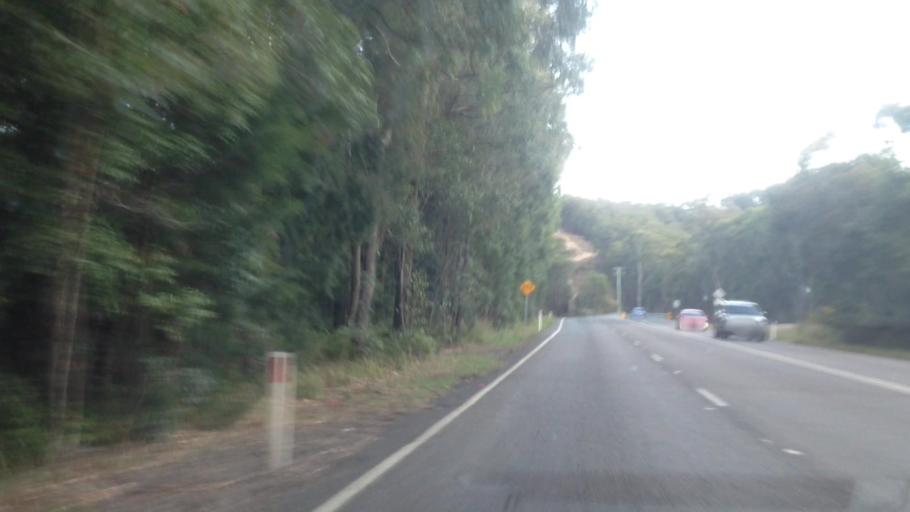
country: AU
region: New South Wales
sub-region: Lake Macquarie Shire
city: Cooranbong
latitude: -32.9615
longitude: 151.4797
